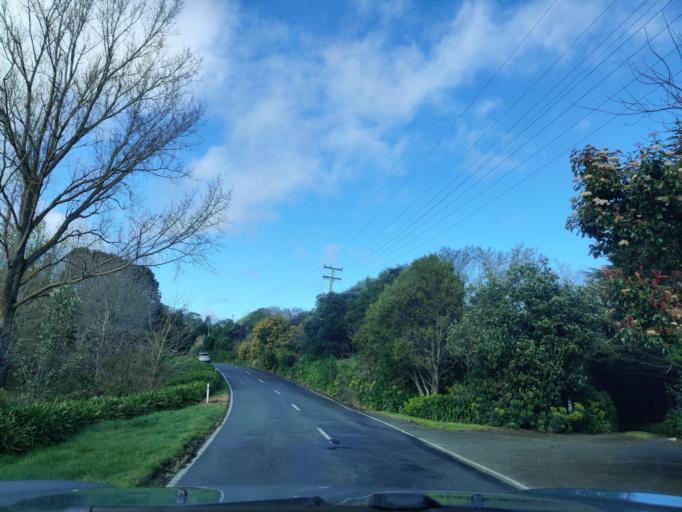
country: NZ
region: Hawke's Bay
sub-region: Hastings District
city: Hastings
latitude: -39.6863
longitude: 176.8982
